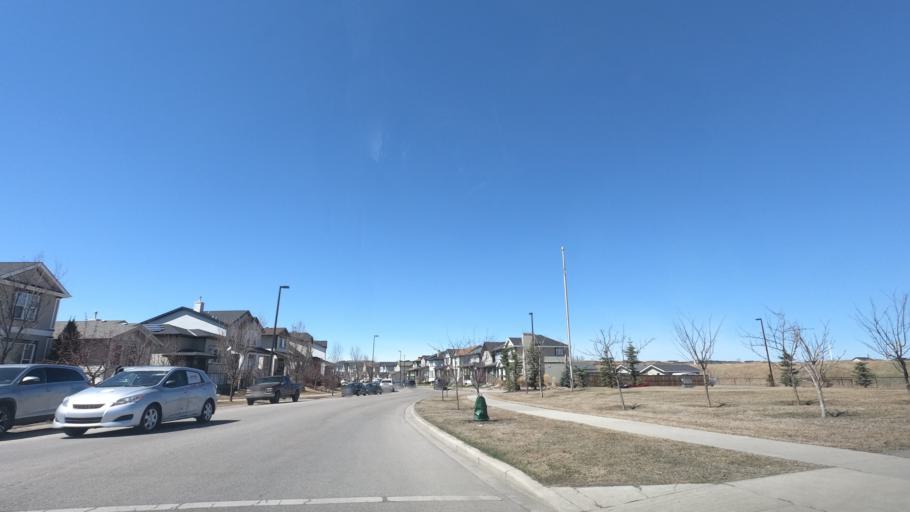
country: CA
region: Alberta
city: Airdrie
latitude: 51.3028
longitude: -114.0410
